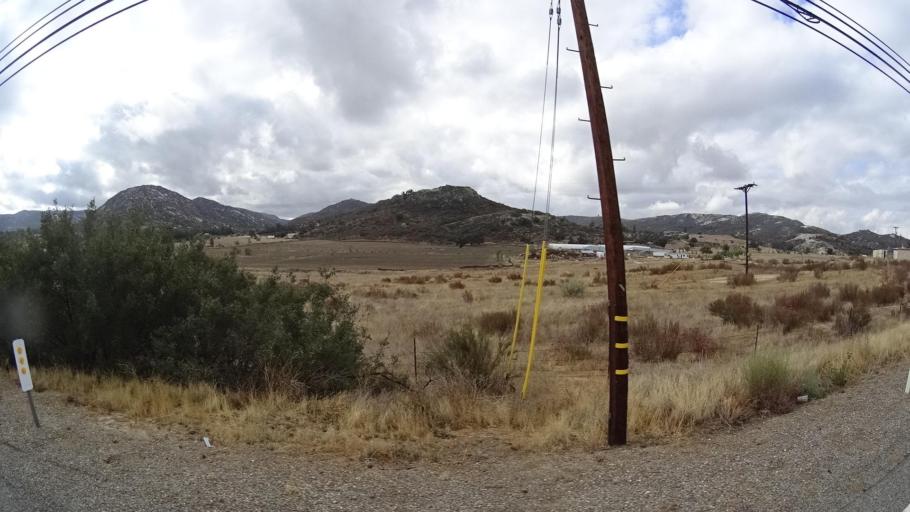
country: US
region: California
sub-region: San Diego County
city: Campo
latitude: 32.6302
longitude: -116.4394
